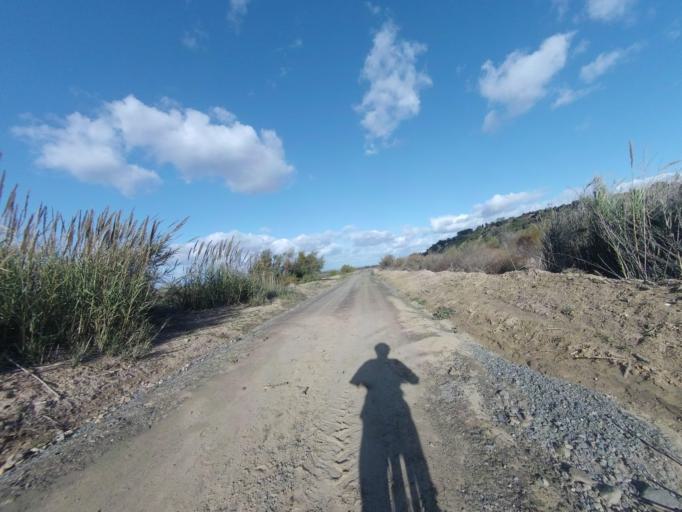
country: ES
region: Andalusia
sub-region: Provincia de Huelva
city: Palos de la Frontera
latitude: 37.2575
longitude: -6.8749
